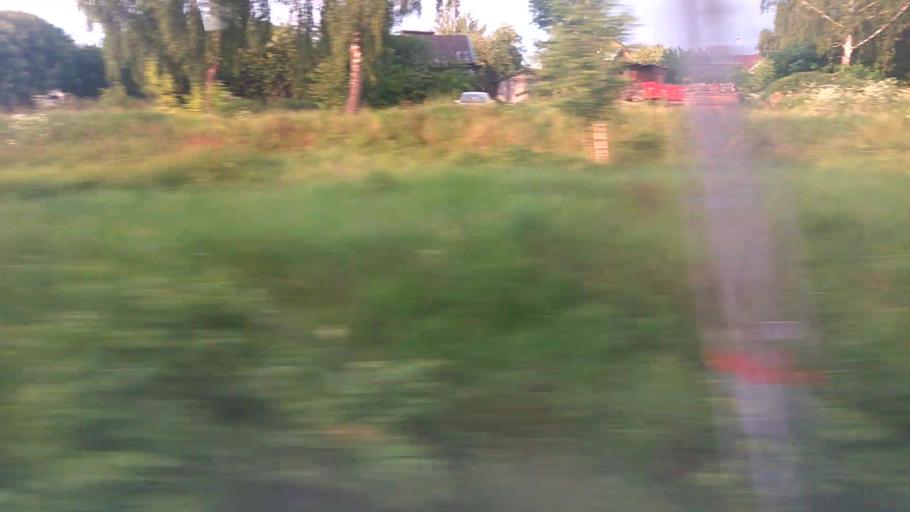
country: RU
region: Moskovskaya
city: Stupino
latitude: 54.8882
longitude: 38.0971
